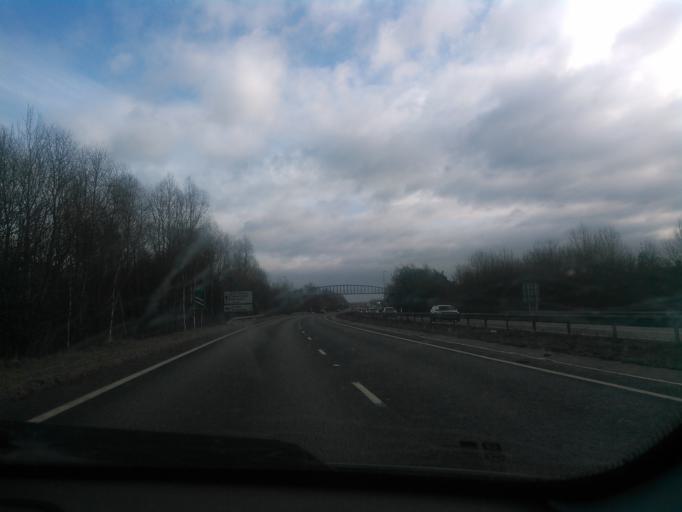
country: GB
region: England
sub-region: Derbyshire
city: Rodsley
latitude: 52.8846
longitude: -1.7282
